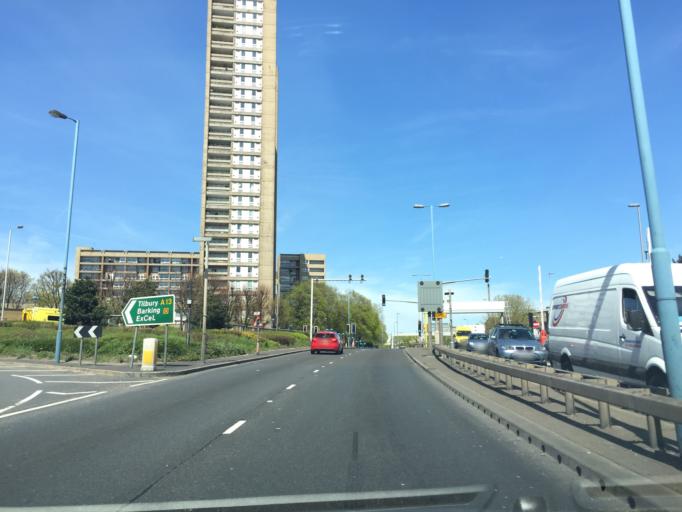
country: GB
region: England
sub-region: Greater London
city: Poplar
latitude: 51.5123
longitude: -0.0083
